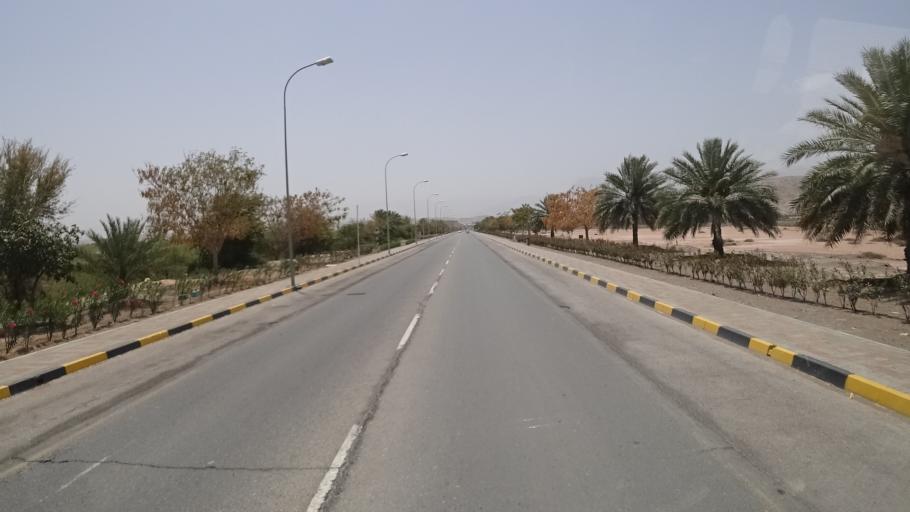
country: OM
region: Muhafazat Masqat
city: Muscat
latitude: 23.2492
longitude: 58.9058
